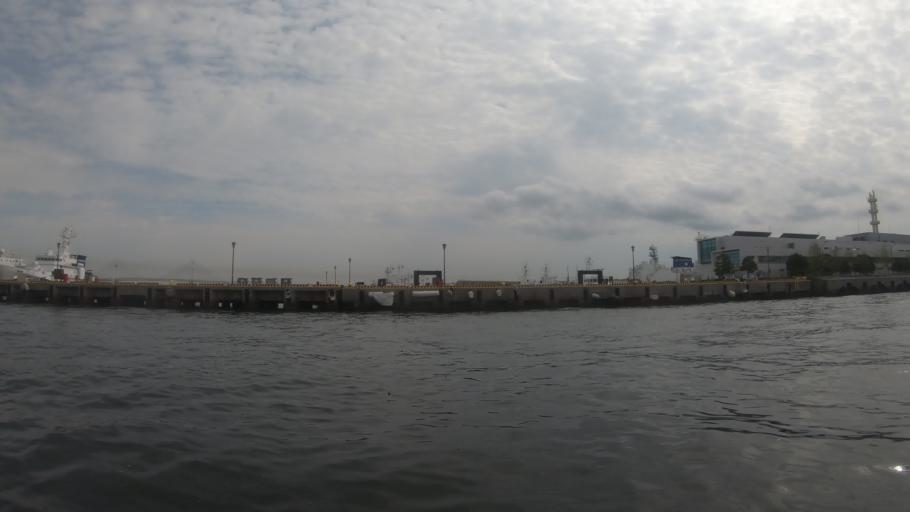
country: JP
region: Kanagawa
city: Yokohama
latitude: 35.4570
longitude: 139.6440
